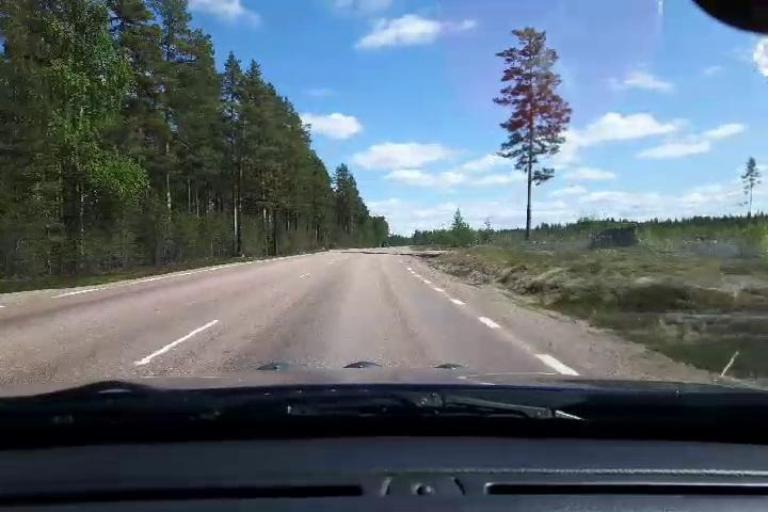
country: SE
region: Gaevleborg
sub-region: Ljusdals Kommun
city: Farila
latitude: 61.9431
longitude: 15.4658
